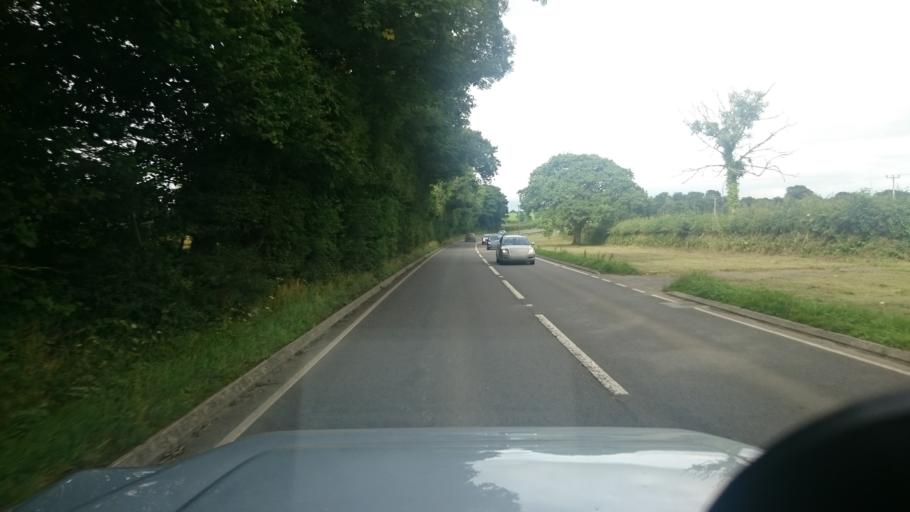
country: GB
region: Wales
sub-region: Pembrokeshire
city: Narberth
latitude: 51.8139
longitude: -4.7423
